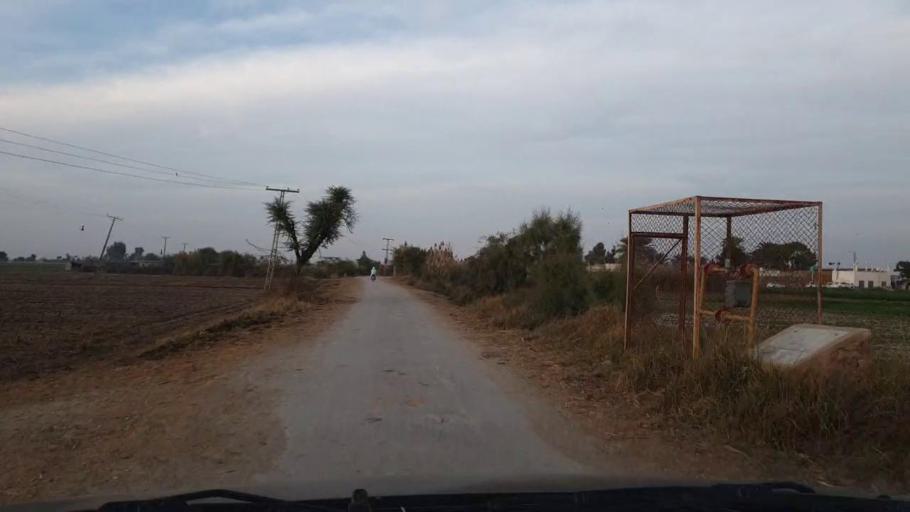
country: PK
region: Sindh
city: Khadro
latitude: 26.1364
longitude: 68.7570
